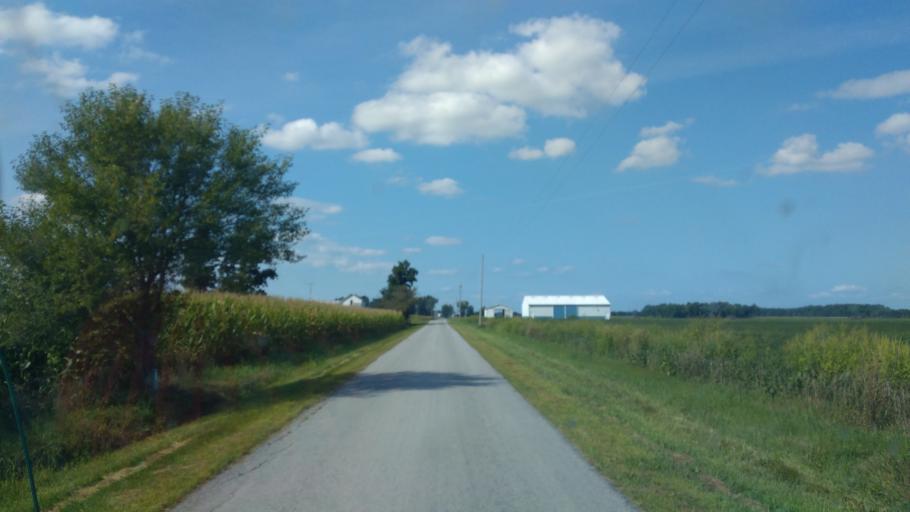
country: US
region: Ohio
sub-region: Hardin County
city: Forest
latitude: 40.7184
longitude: -83.4779
